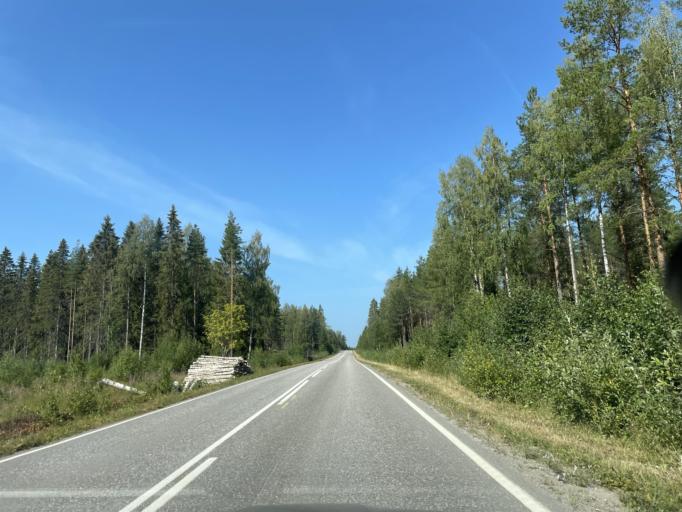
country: FI
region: Central Finland
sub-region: Saarijaervi-Viitasaari
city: Pihtipudas
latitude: 63.3680
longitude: 25.6263
